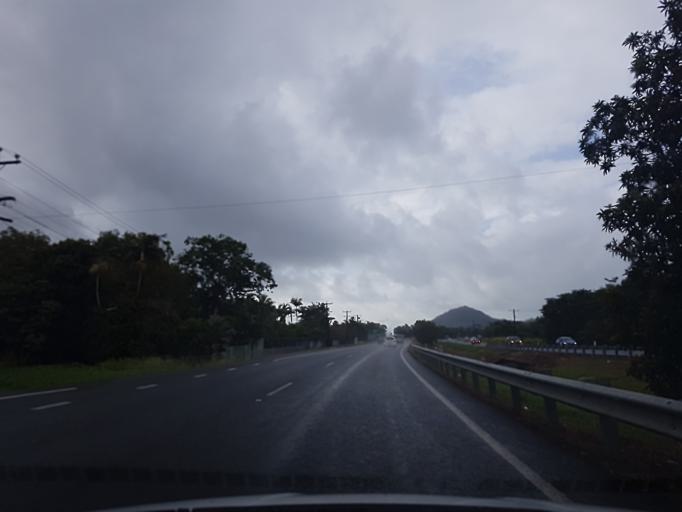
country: AU
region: Queensland
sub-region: Cairns
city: Yorkeys Knob
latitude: -16.8257
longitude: 145.6922
